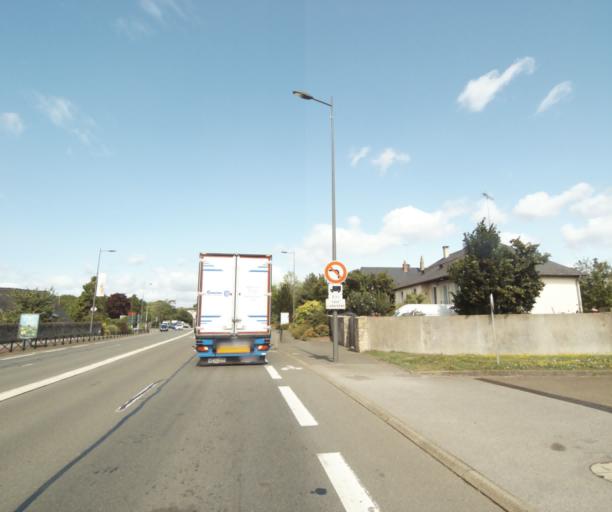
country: FR
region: Pays de la Loire
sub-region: Departement de la Sarthe
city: Sable-sur-Sarthe
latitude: 47.8436
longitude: -0.3317
